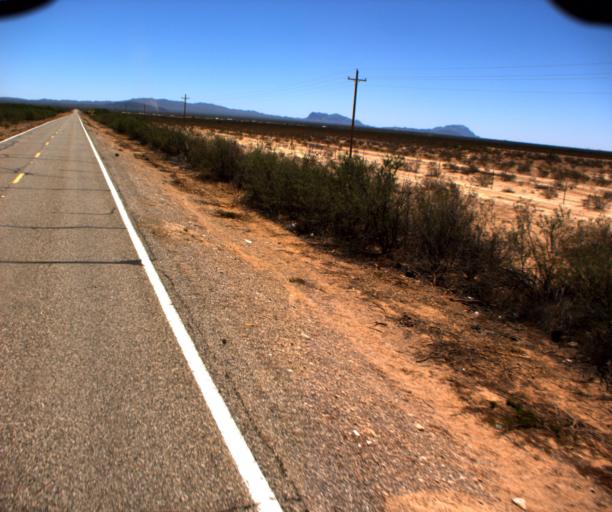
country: US
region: Arizona
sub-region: Pima County
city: Ajo
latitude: 32.1871
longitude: -112.3857
